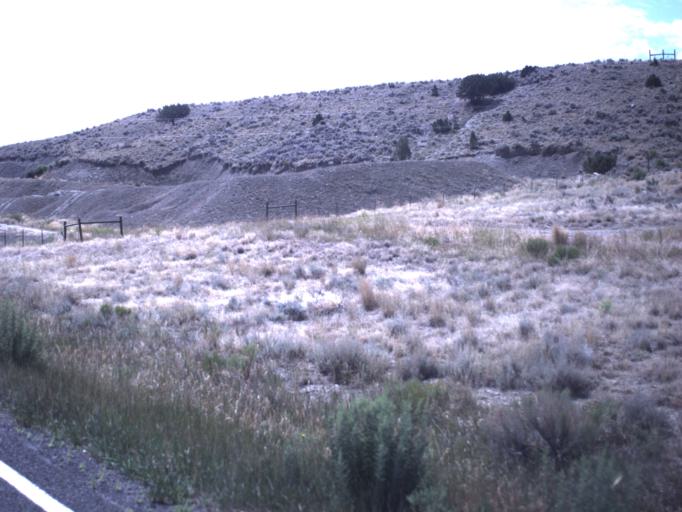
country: US
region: Utah
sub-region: Daggett County
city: Manila
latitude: 40.9726
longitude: -109.7184
